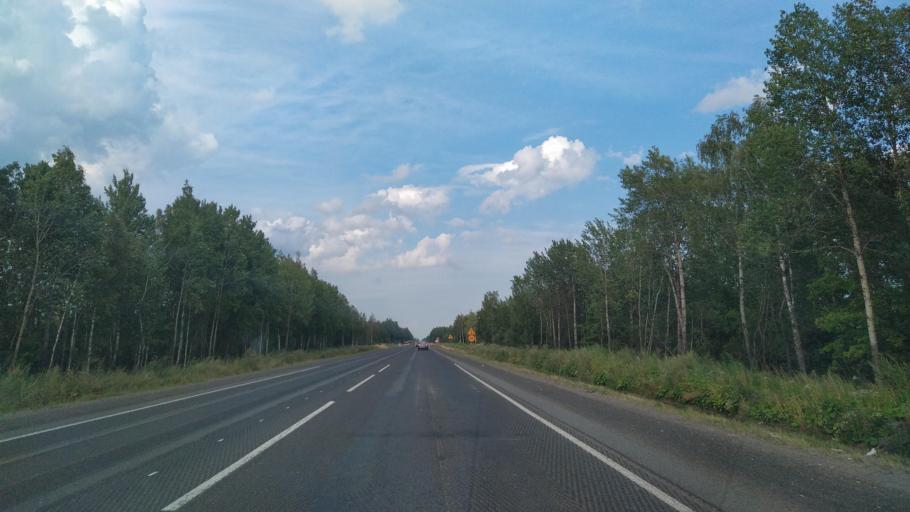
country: RU
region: Novgorod
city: Shimsk
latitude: 58.2903
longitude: 30.8584
